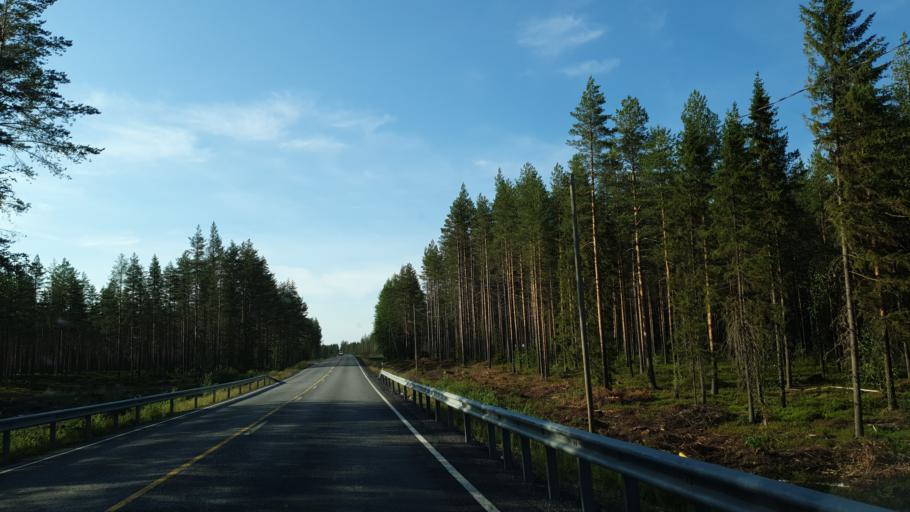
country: FI
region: Kainuu
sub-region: Kehys-Kainuu
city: Kuhmo
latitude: 64.0869
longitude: 29.4828
